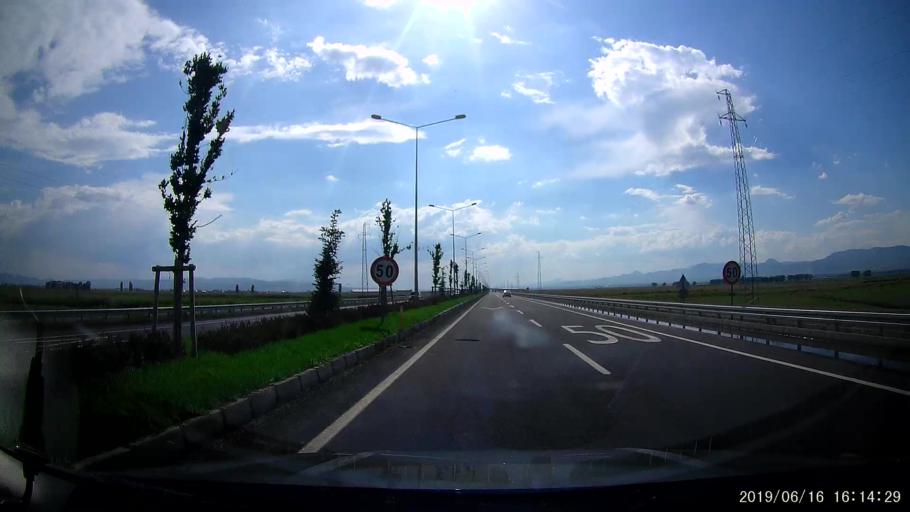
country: TR
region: Erzurum
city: Erzurum
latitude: 39.9607
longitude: 41.2475
